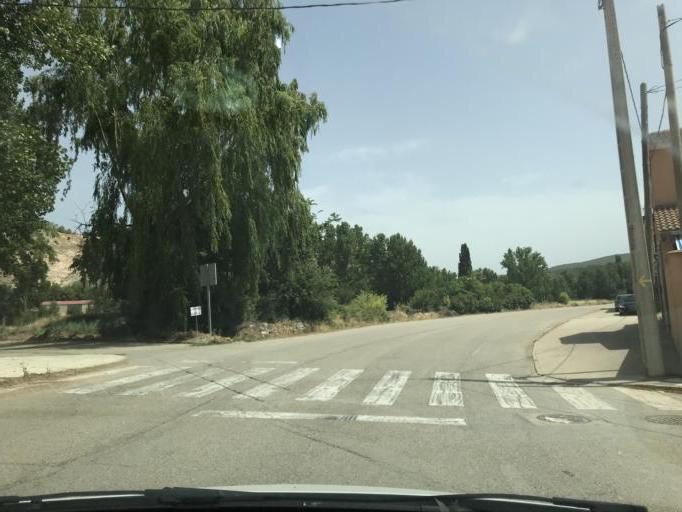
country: ES
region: Castille-La Mancha
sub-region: Provincia de Cuenca
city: Torralba
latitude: 40.3043
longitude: -2.2860
